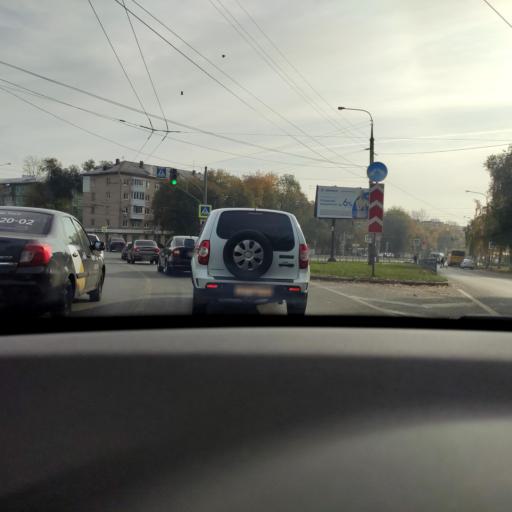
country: RU
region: Samara
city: Samara
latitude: 53.2124
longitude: 50.2269
